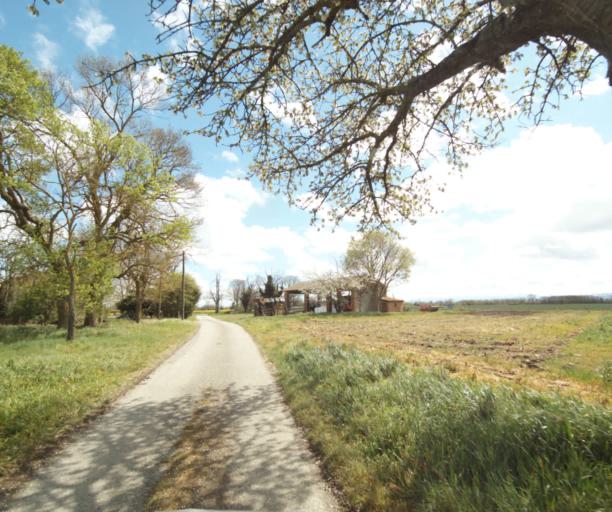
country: FR
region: Midi-Pyrenees
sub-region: Departement de l'Ariege
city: Saverdun
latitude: 43.2648
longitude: 1.5932
